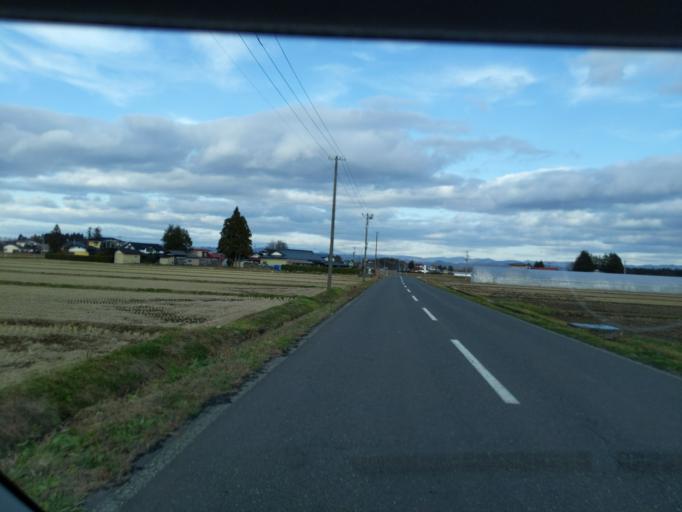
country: JP
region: Iwate
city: Mizusawa
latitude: 39.1755
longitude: 141.0952
